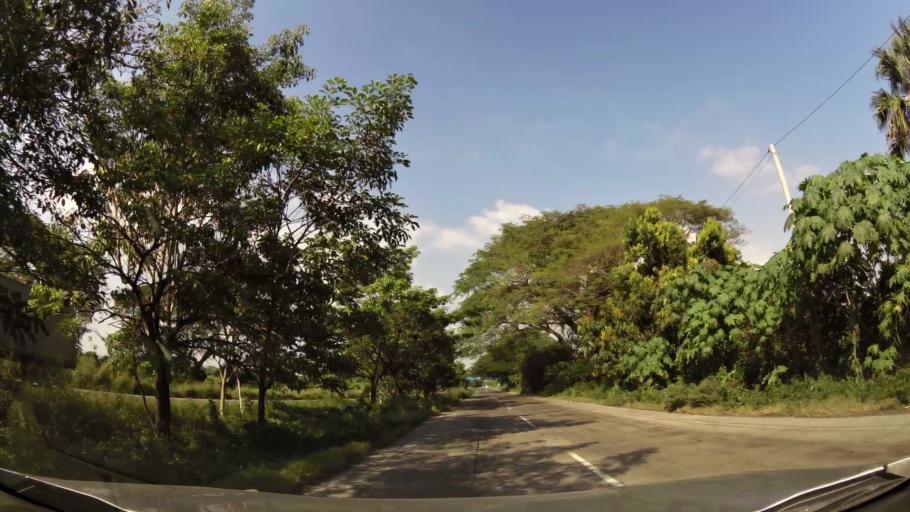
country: GT
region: Escuintla
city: Puerto San Jose
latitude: 14.0062
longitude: -90.7861
